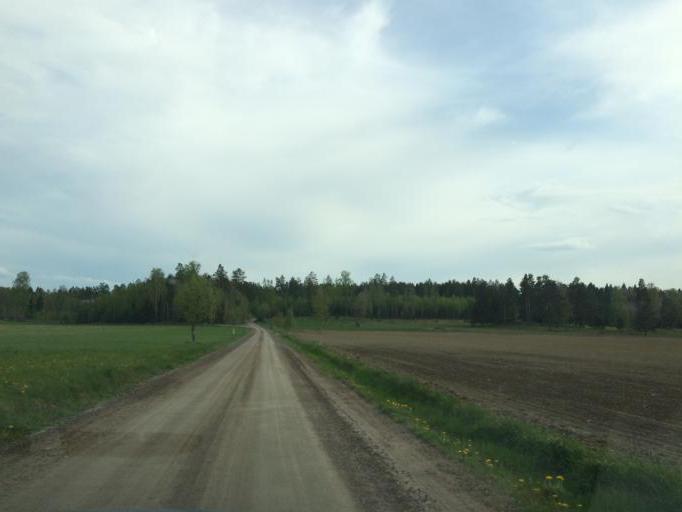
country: SE
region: Vaestmanland
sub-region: Kopings Kommun
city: Koping
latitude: 59.6083
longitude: 16.0770
